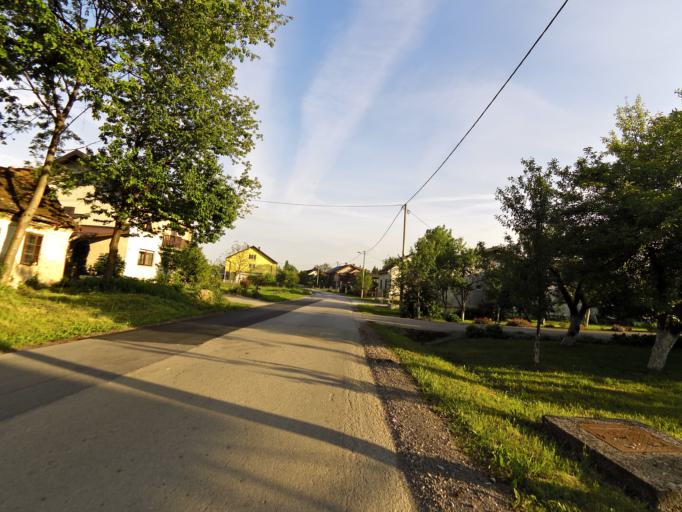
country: HR
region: Karlovacka
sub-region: Grad Karlovac
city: Karlovac
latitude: 45.5051
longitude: 15.5315
